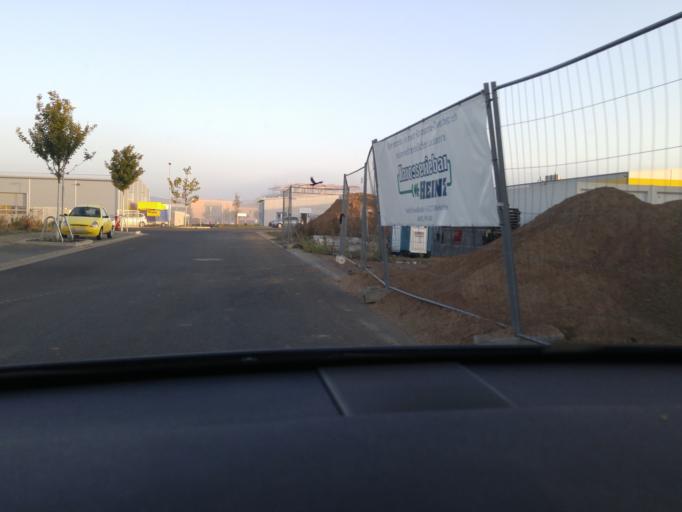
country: DE
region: Hesse
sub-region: Regierungsbezirk Darmstadt
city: Friedberg
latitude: 50.3520
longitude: 8.7550
